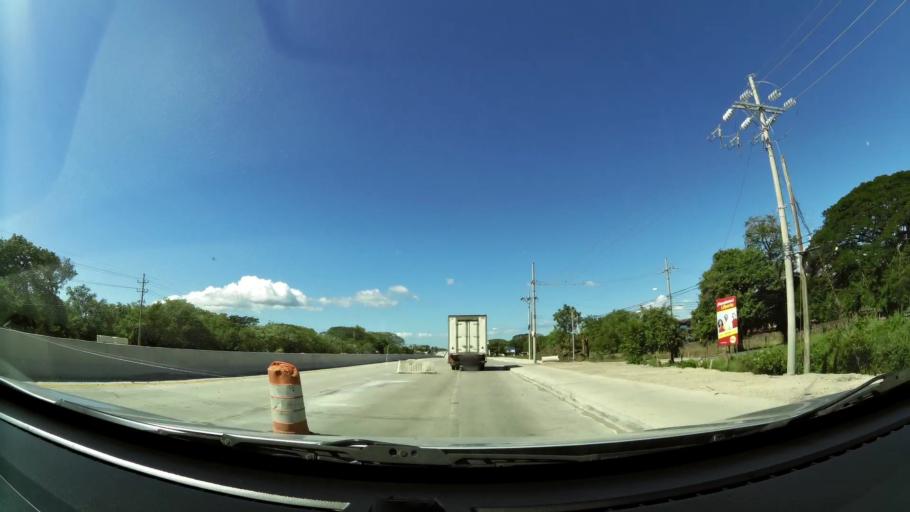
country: CR
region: Guanacaste
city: Liberia
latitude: 10.6216
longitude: -85.4403
